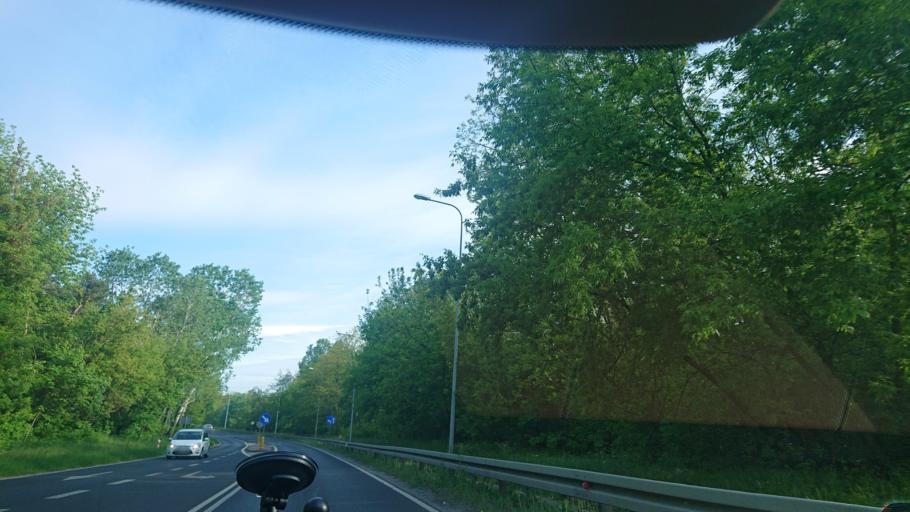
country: PL
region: Greater Poland Voivodeship
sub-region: Powiat gnieznienski
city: Gniezno
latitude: 52.5192
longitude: 17.5831
